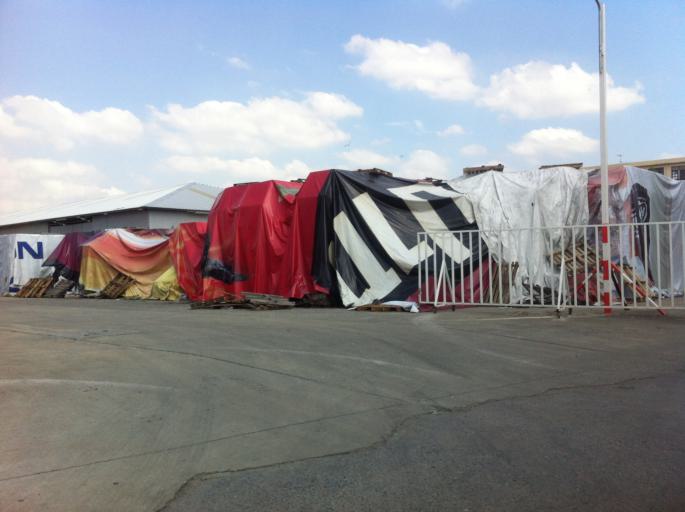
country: TH
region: Bangkok
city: Bang Na
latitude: 13.6569
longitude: 100.6401
